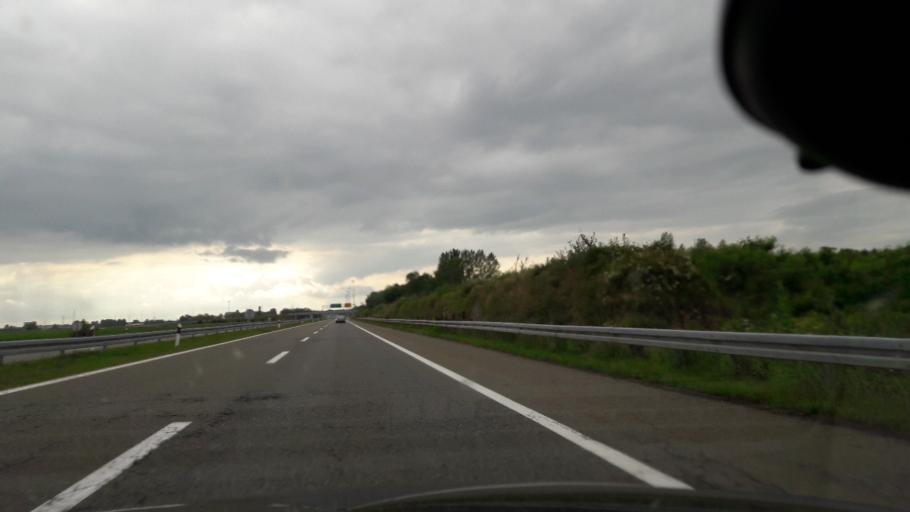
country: HR
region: Vukovarsko-Srijemska
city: Zupanja
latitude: 45.0998
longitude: 18.7239
